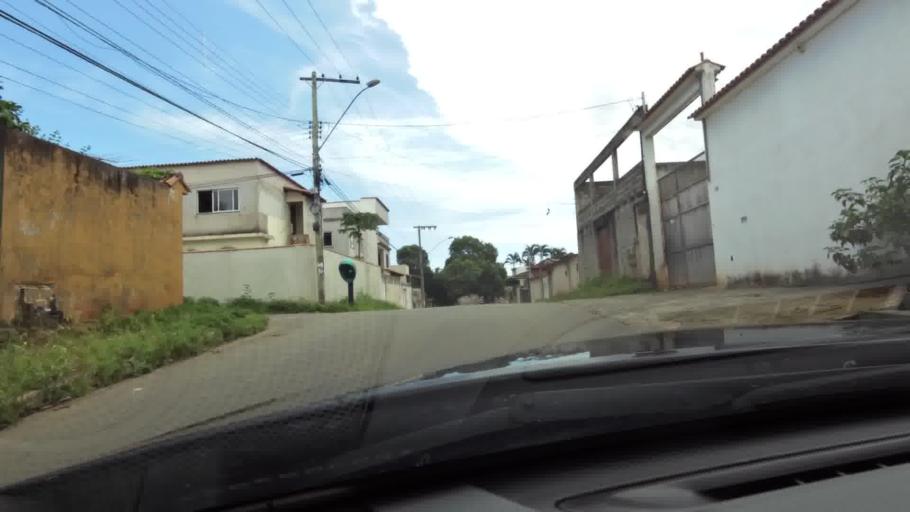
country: BR
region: Espirito Santo
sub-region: Guarapari
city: Guarapari
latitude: -20.6502
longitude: -40.5020
